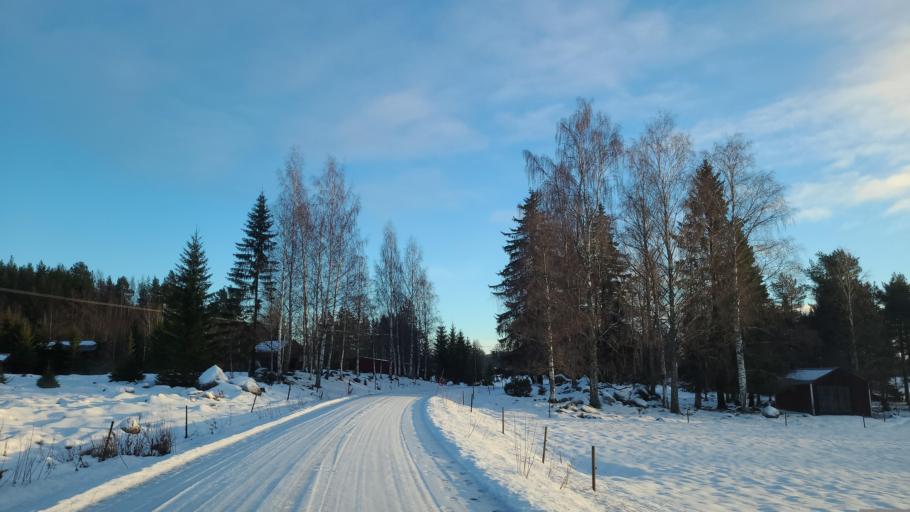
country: SE
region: Gaevleborg
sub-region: Bollnas Kommun
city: Kilafors
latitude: 61.3990
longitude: 16.6639
